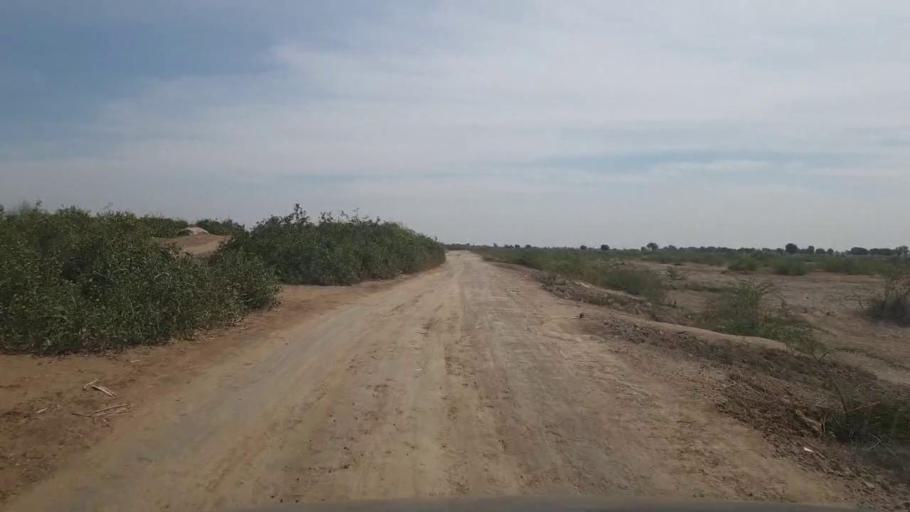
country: PK
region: Sindh
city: Kunri
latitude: 25.2927
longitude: 69.5847
